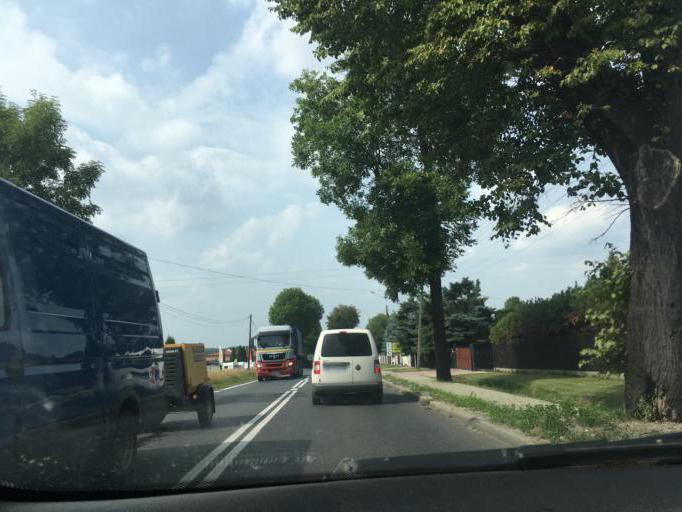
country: PL
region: Silesian Voivodeship
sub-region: Powiat bierunsko-ledzinski
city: Bojszowy
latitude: 50.0835
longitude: 19.1397
